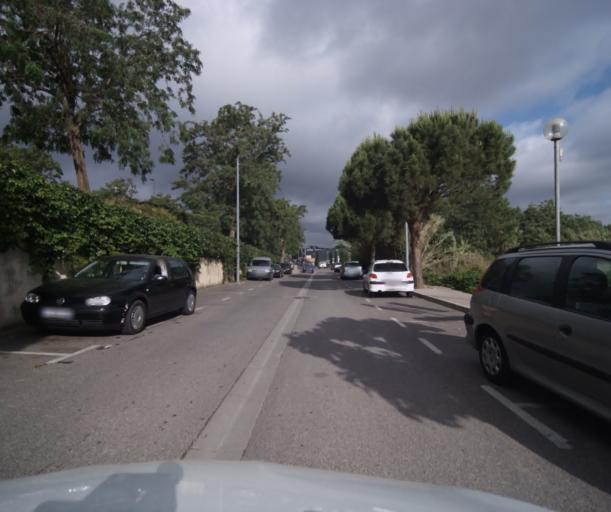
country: FR
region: Provence-Alpes-Cote d'Azur
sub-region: Departement du Var
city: Sanary-sur-Mer
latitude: 43.1228
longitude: 5.8251
